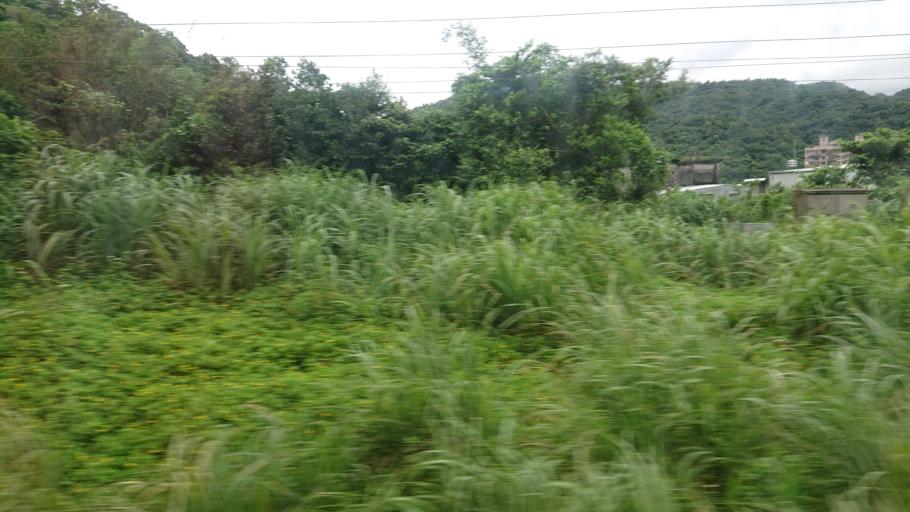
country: TW
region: Taiwan
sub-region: Keelung
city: Keelung
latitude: 25.1067
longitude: 121.8224
